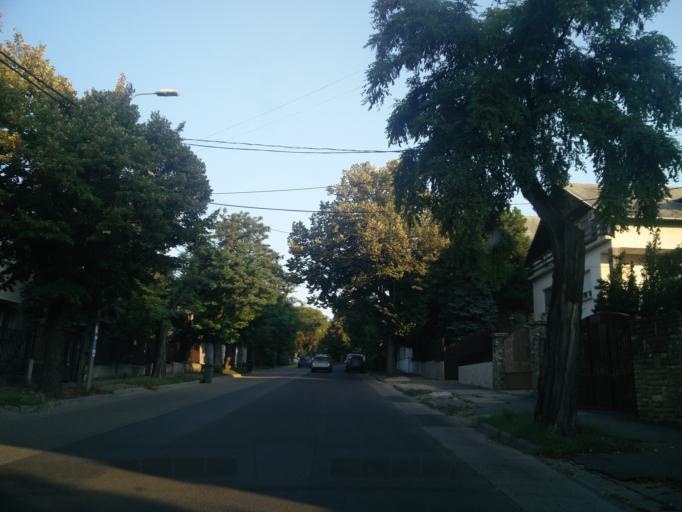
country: HU
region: Budapest
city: Budapest XII. keruelet
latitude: 47.4693
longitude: 19.0133
